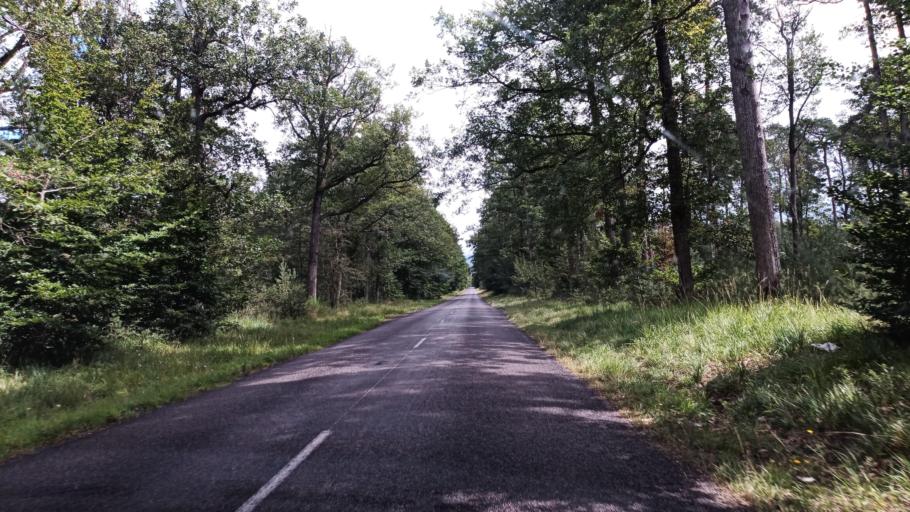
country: FR
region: Ile-de-France
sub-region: Departement de Seine-et-Marne
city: Avon
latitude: 48.3713
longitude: 2.7249
